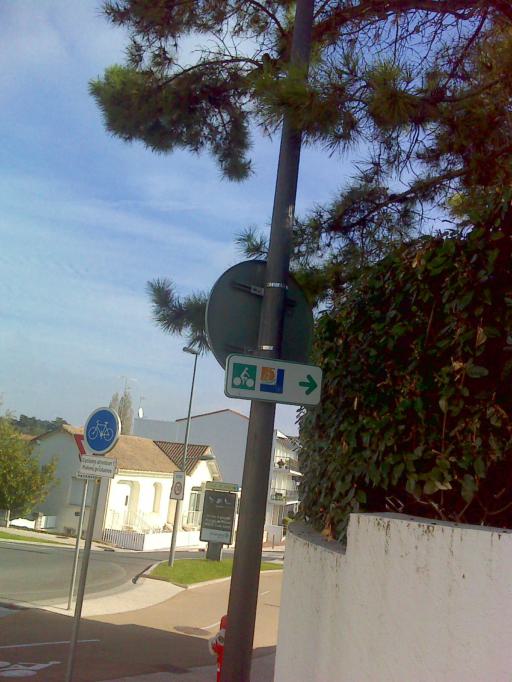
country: FR
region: Poitou-Charentes
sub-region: Departement de la Charente-Maritime
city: Saint-Palais-sur-Mer
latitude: 45.6389
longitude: -1.0802
